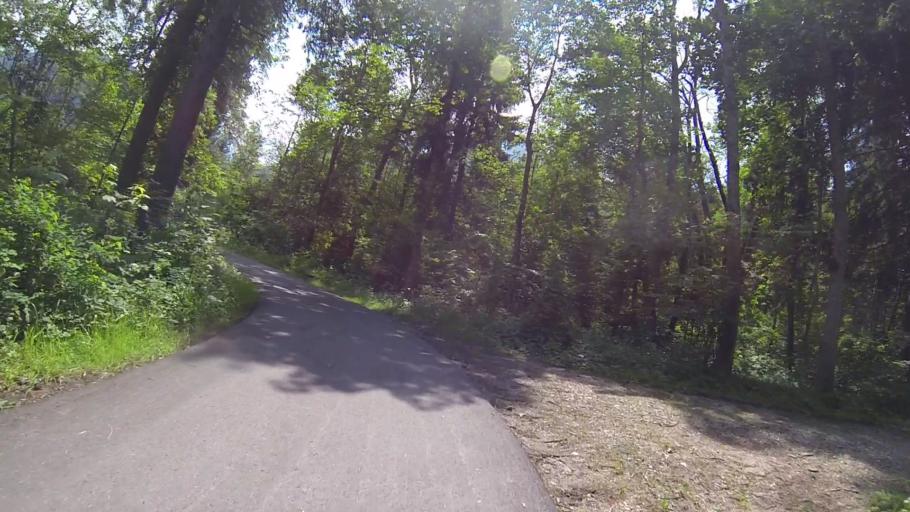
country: DE
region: Bavaria
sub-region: Swabia
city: Schwangau
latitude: 47.5596
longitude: 10.7315
